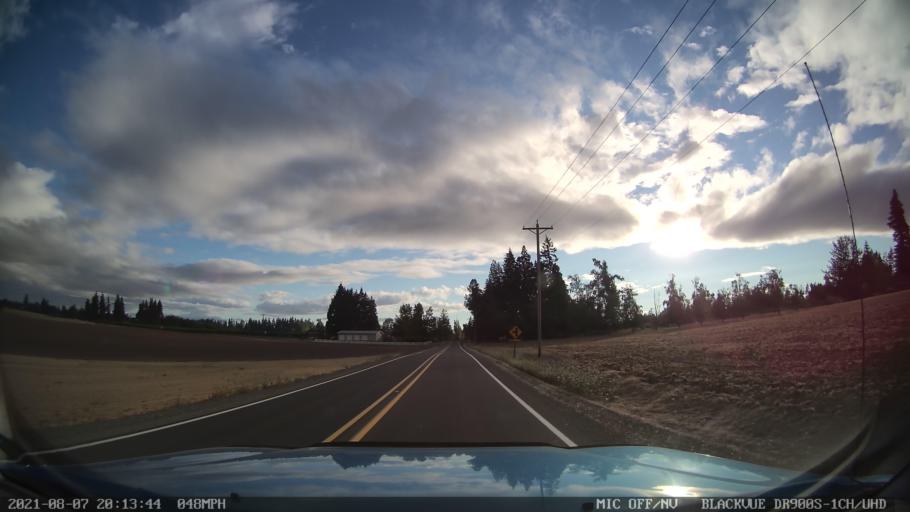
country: US
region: Oregon
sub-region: Marion County
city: Hayesville
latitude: 44.9563
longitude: -122.9283
